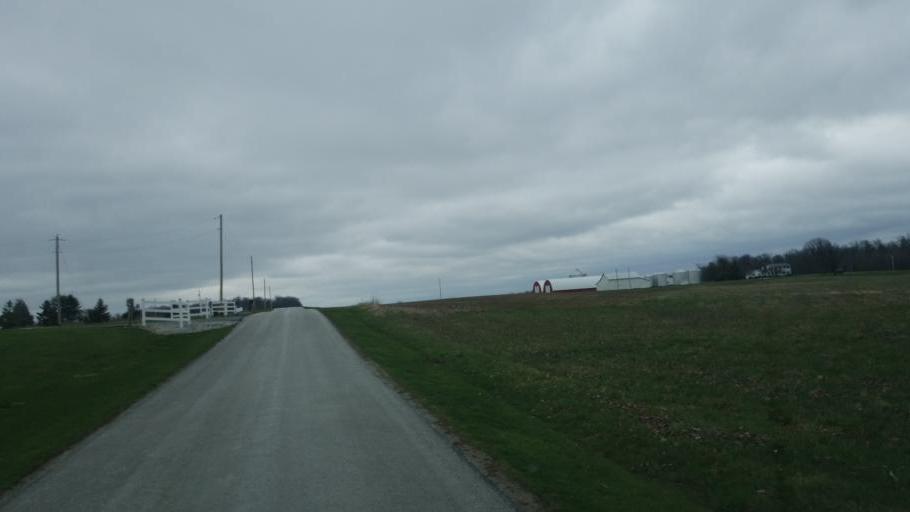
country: US
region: Ohio
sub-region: Hardin County
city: Forest
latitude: 40.6584
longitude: -83.4427
